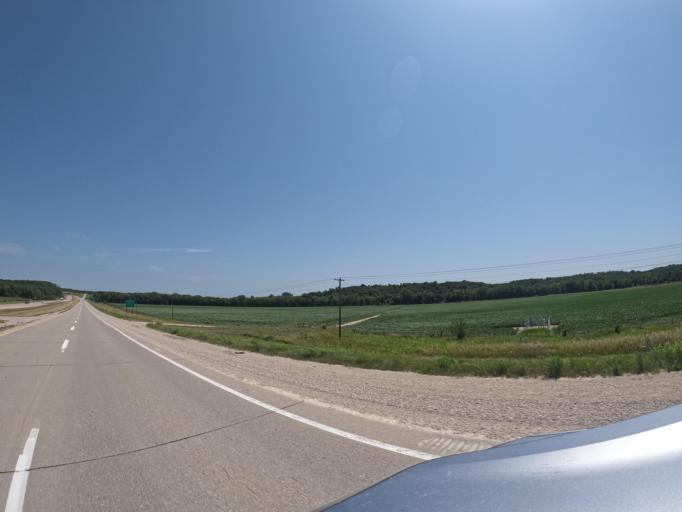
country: US
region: Iowa
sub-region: Henry County
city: Mount Pleasant
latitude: 40.9726
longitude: -91.6518
